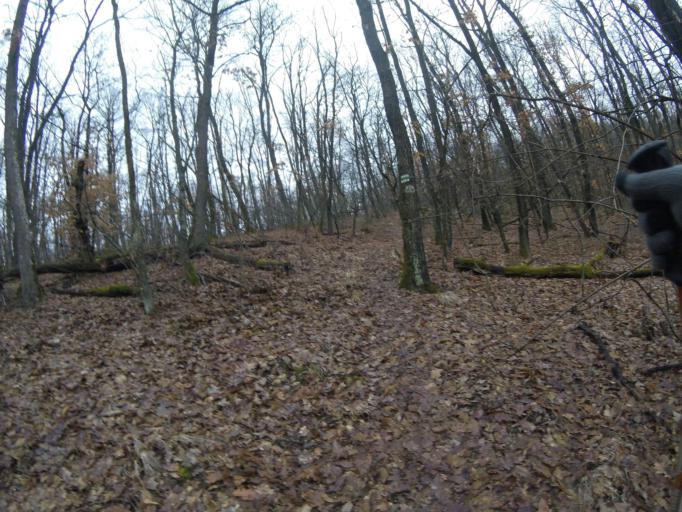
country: HU
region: Borsod-Abauj-Zemplen
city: Rudabanya
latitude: 48.4558
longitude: 20.5705
